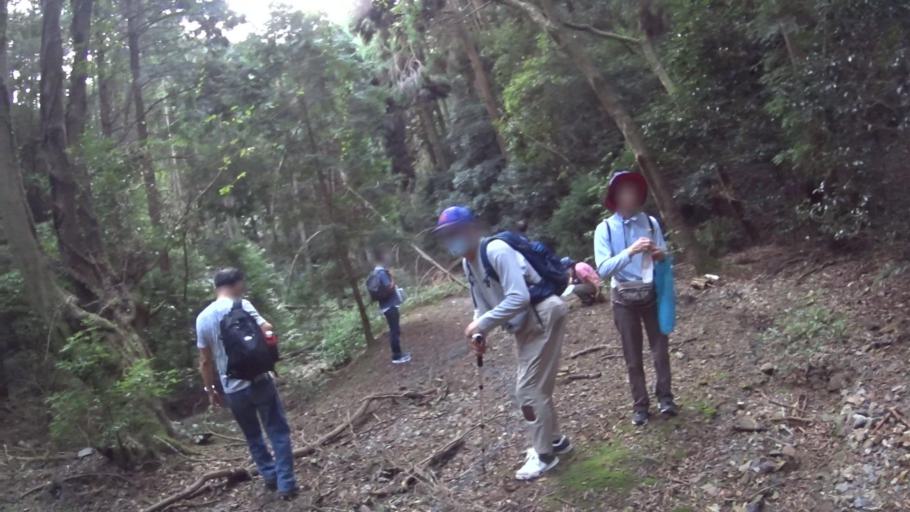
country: JP
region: Osaka
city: Kaizuka
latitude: 34.4812
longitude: 135.3136
